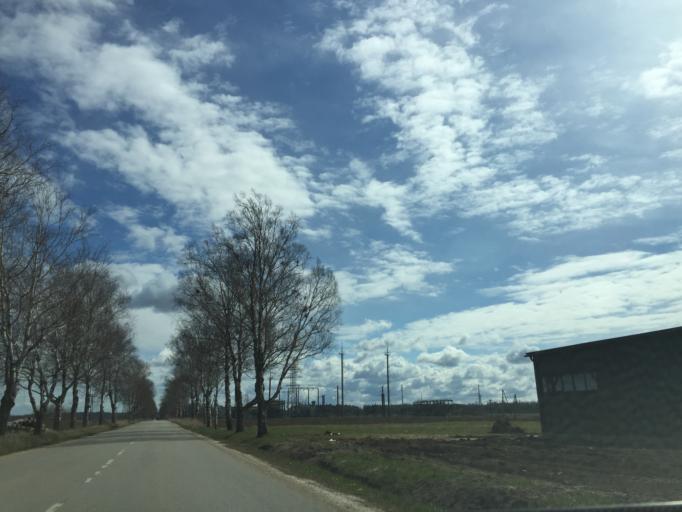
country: LV
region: Salacgrivas
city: Salacgriva
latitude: 57.7482
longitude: 24.3719
